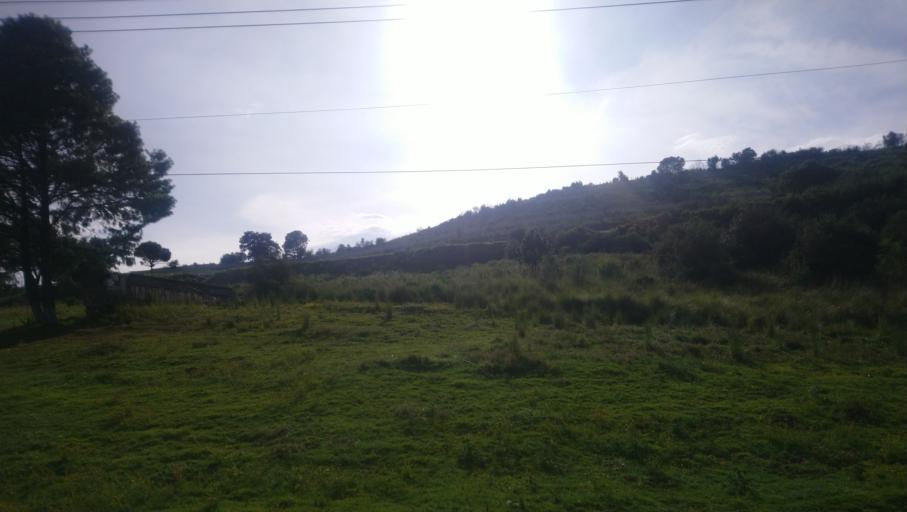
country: MX
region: Mexico
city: Juchitepec de Mariano Riva Palacio
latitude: 19.1261
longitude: -98.9374
